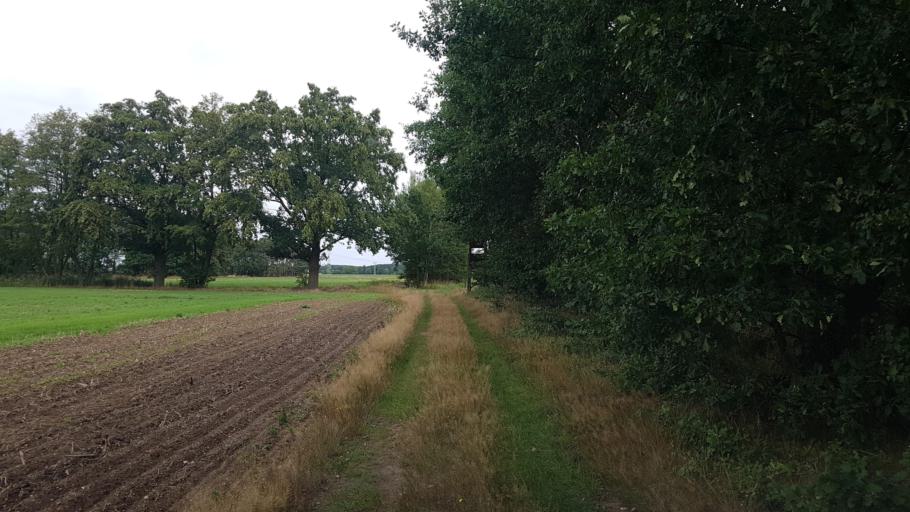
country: DE
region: Brandenburg
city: Schonewalde
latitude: 51.6439
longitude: 13.6067
